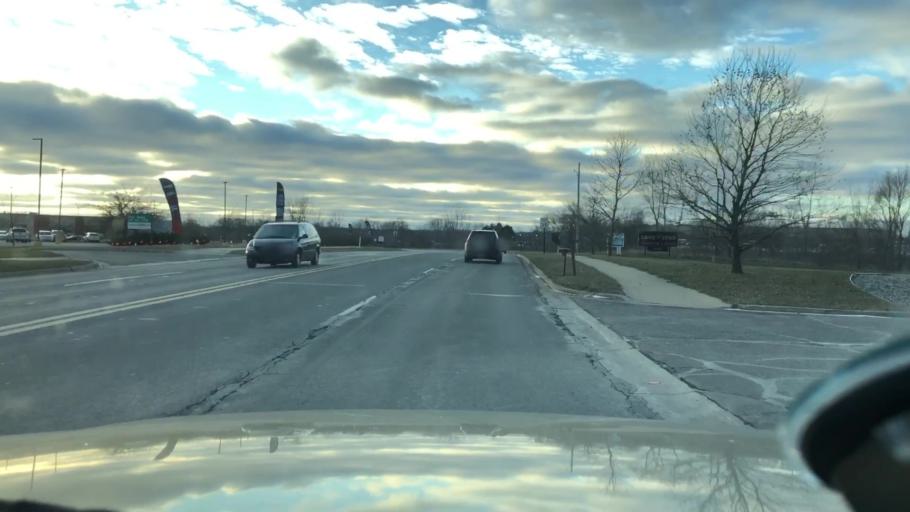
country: US
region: Michigan
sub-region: Jackson County
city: Jackson
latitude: 42.2667
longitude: -84.4557
